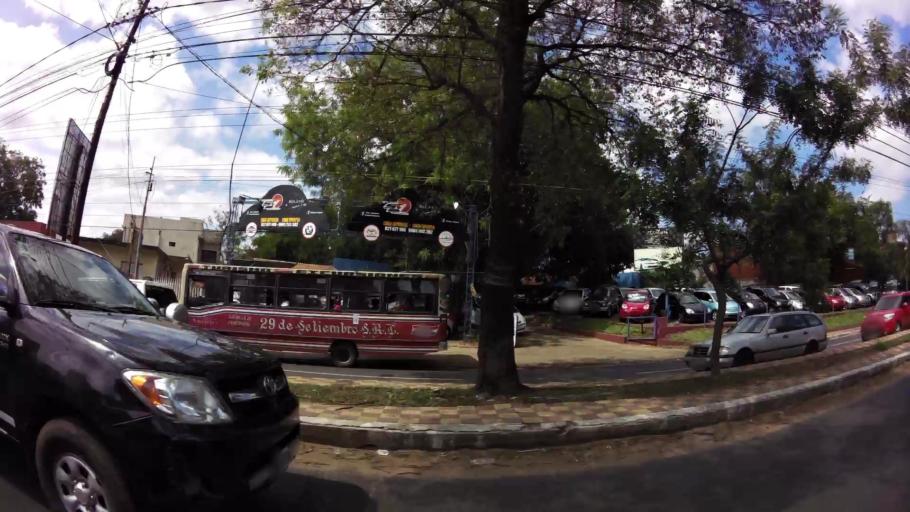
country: PY
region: Central
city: Fernando de la Mora
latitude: -25.3188
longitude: -57.5250
